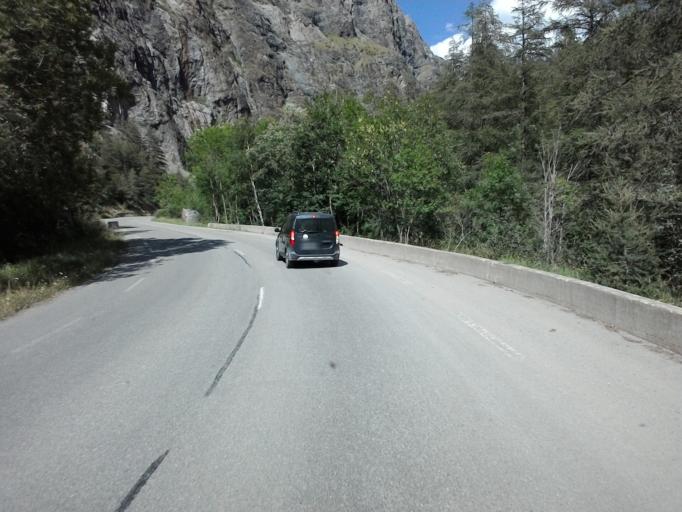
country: FR
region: Rhone-Alpes
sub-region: Departement de l'Isere
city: Mont-de-Lans
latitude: 45.0399
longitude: 6.2595
